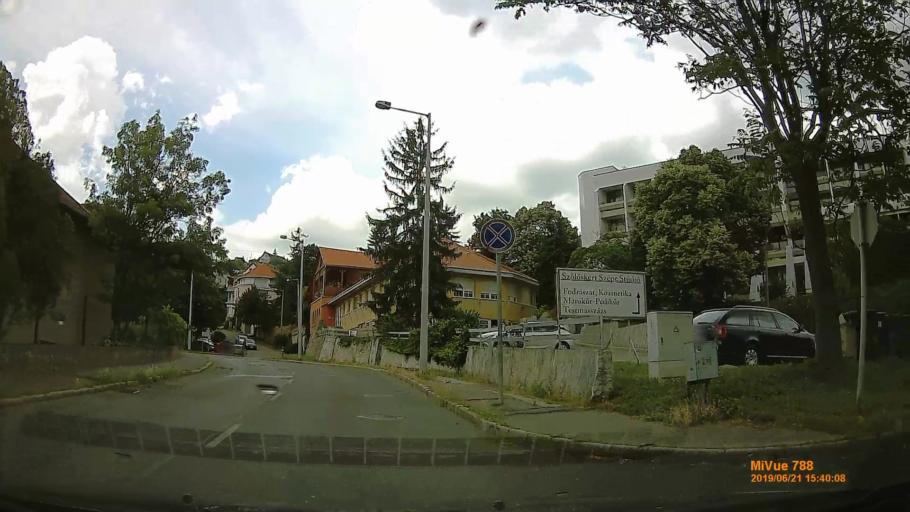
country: HU
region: Baranya
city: Pecs
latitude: 46.0823
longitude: 18.2155
